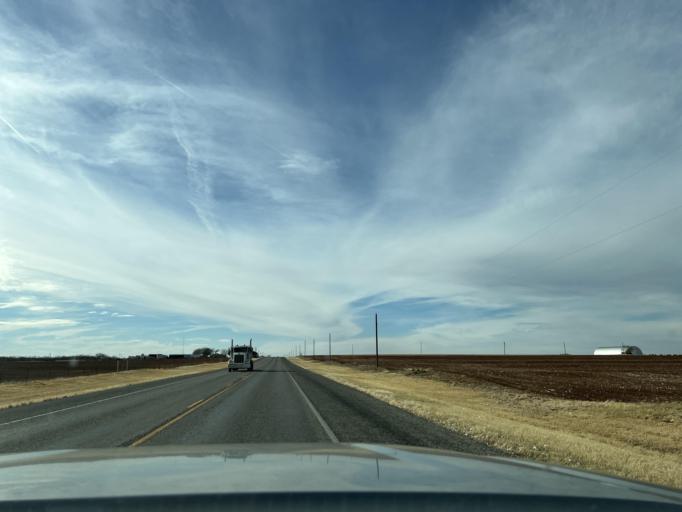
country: US
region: Texas
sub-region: Jones County
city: Anson
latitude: 32.7519
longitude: -99.9410
